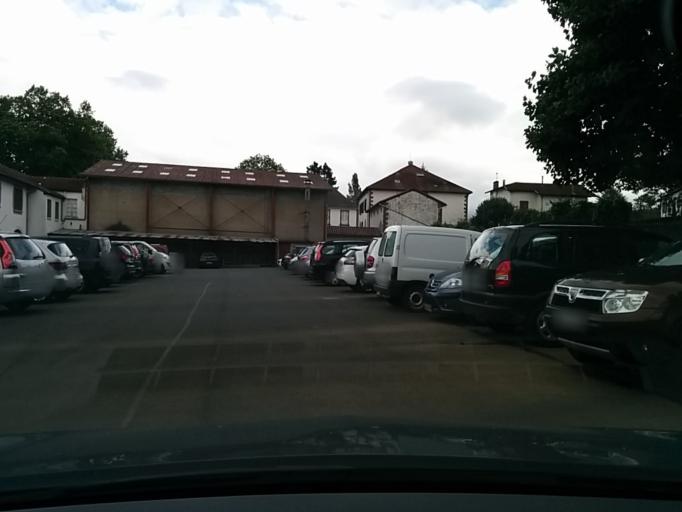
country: FR
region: Aquitaine
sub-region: Departement des Pyrenees-Atlantiques
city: Saint-Jean-Pied-de-Port
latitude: 43.1605
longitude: -1.2397
